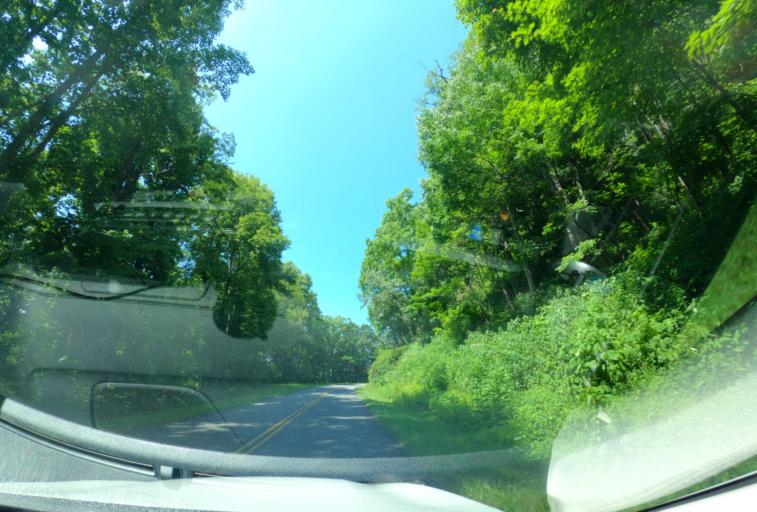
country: US
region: North Carolina
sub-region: Haywood County
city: Maggie Valley
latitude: 35.4415
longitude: -83.0926
